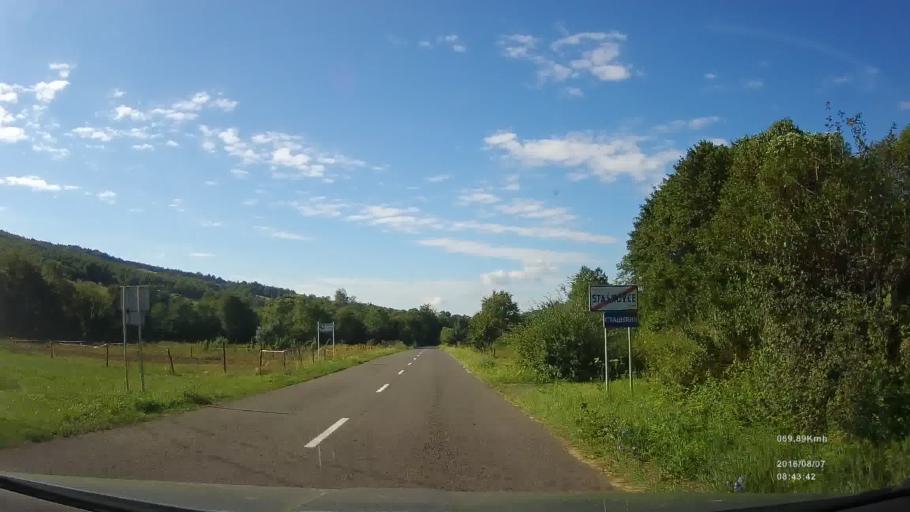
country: SK
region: Presovsky
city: Stropkov
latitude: 49.2750
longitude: 21.7517
